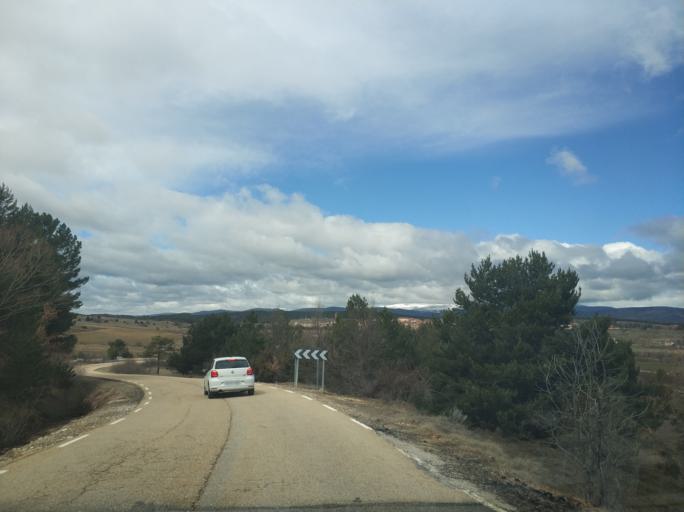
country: ES
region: Castille and Leon
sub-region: Provincia de Soria
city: Abejar
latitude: 41.7987
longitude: -2.7796
